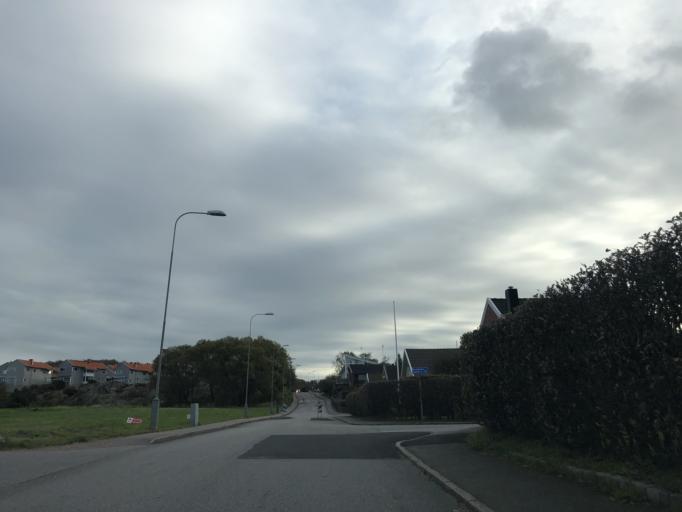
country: SE
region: Vaestra Goetaland
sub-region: Goteborg
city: Majorna
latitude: 57.6798
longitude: 11.8750
